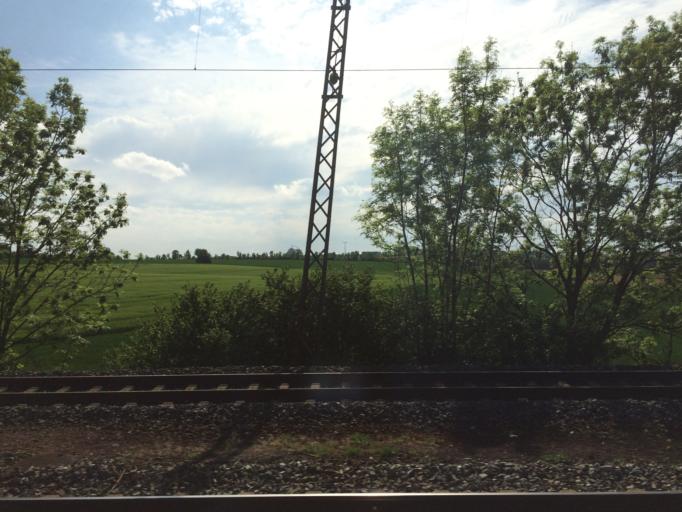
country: DE
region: Bavaria
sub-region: Regierungsbezirk Unterfranken
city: Biebelried
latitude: 49.7896
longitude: 10.0888
